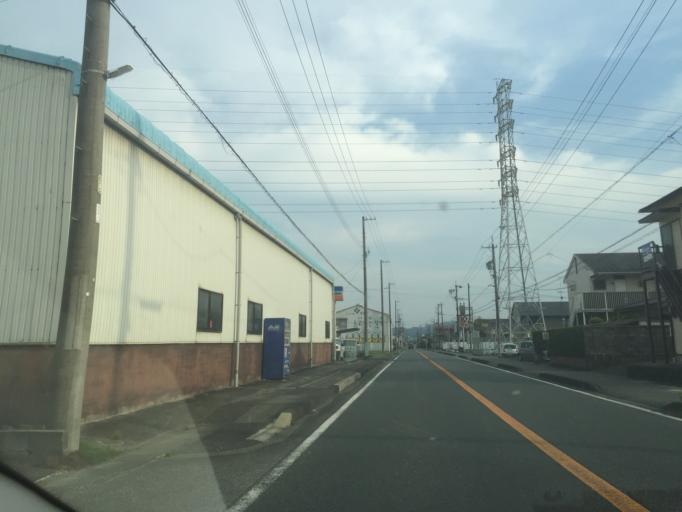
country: JP
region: Shizuoka
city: Kakegawa
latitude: 34.7986
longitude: 138.0126
